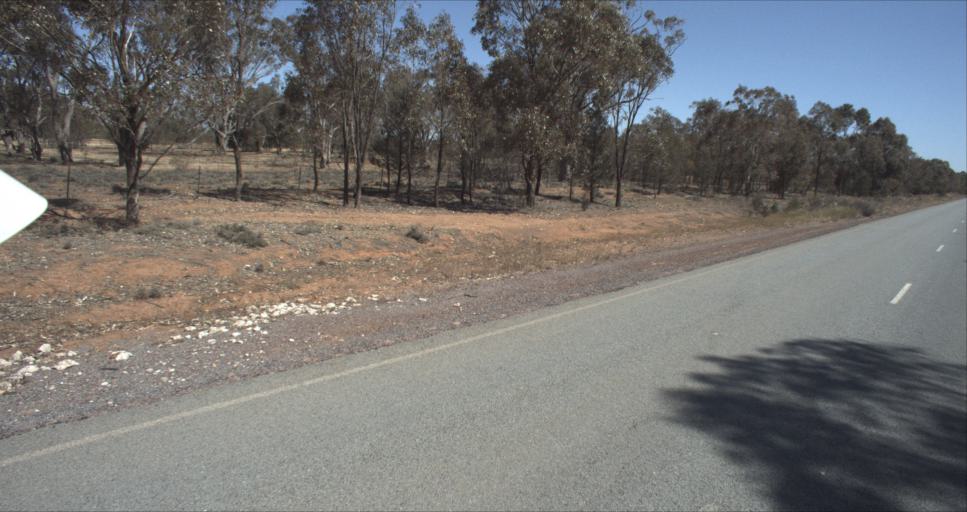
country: AU
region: New South Wales
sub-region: Leeton
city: Leeton
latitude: -34.4907
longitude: 146.4652
